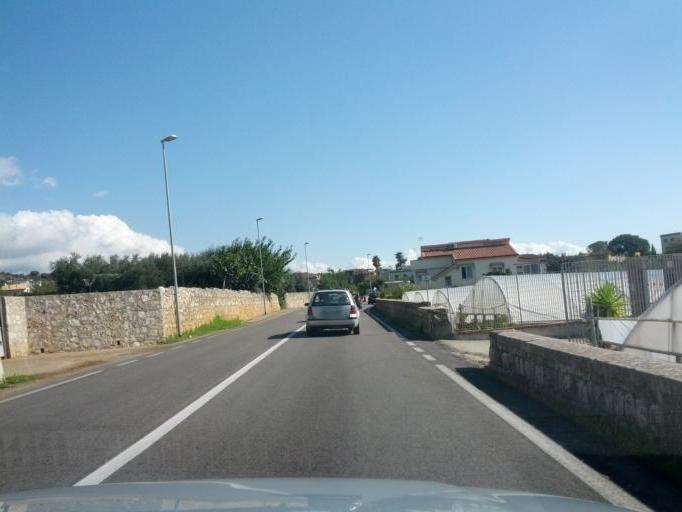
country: IT
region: Latium
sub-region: Provincia di Latina
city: Gaeta
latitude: 41.2518
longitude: 13.5808
